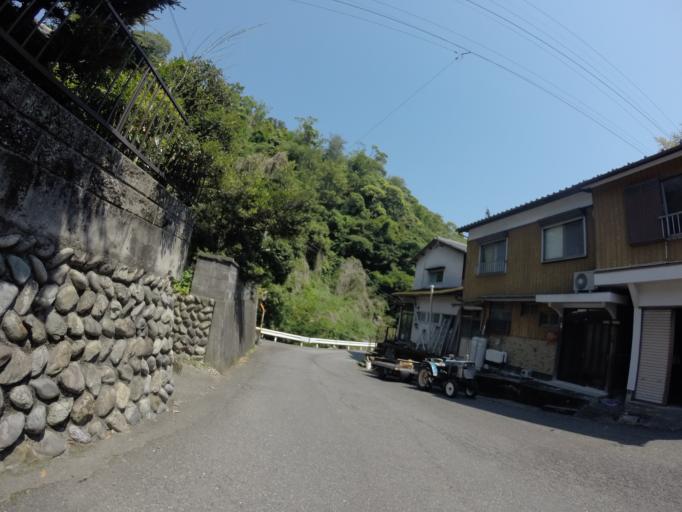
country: JP
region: Shizuoka
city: Fujinomiya
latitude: 35.1201
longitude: 138.5925
